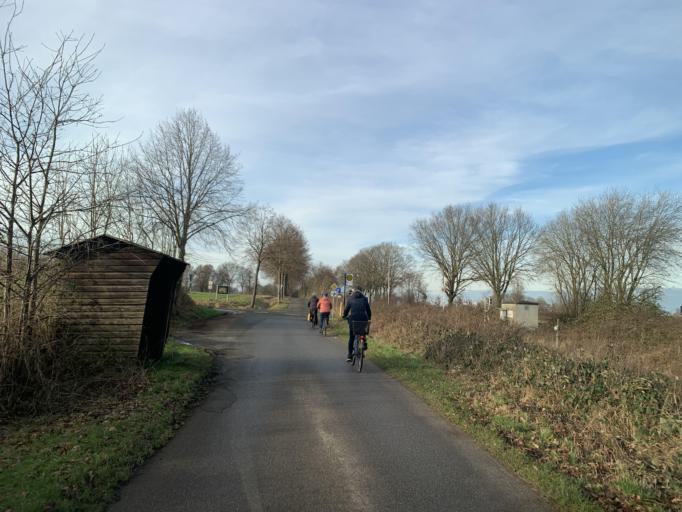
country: DE
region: North Rhine-Westphalia
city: Ludinghausen
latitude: 51.7917
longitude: 7.3848
